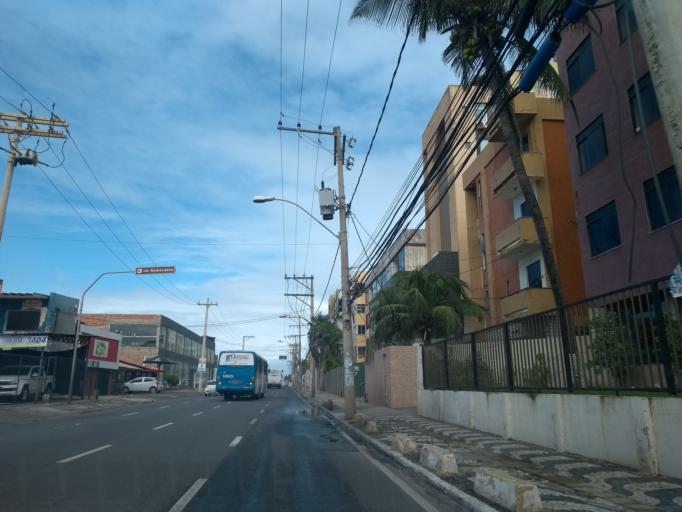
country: BR
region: Bahia
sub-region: Salvador
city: Salvador
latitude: -13.0001
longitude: -38.4504
